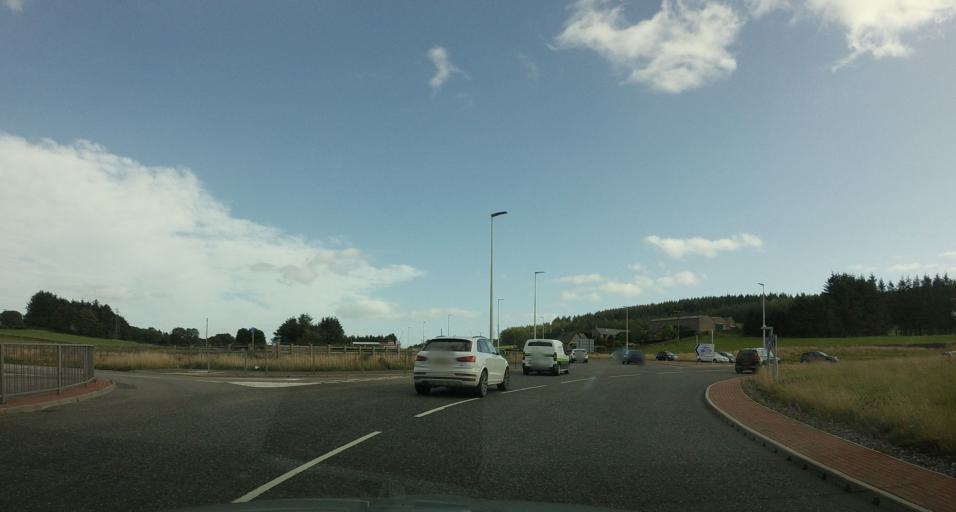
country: GB
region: Scotland
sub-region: Aberdeenshire
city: Westhill
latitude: 57.1477
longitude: -2.2421
